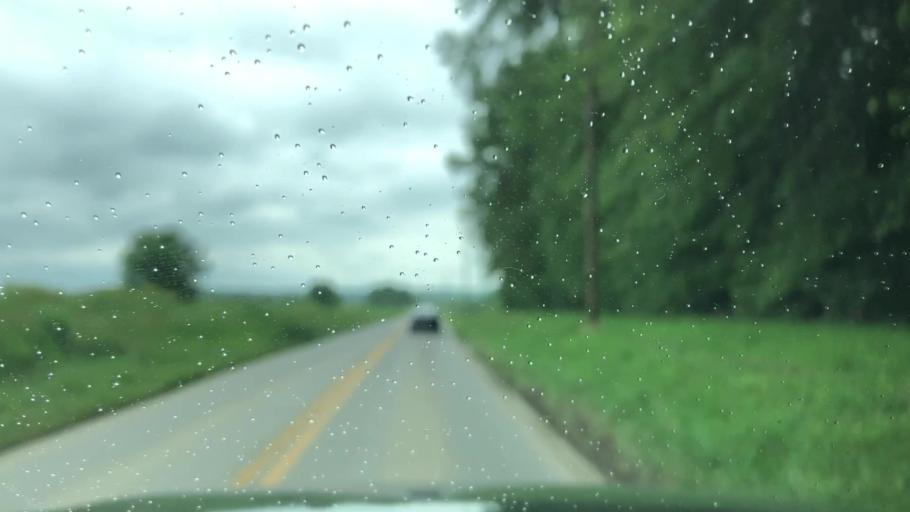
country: US
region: Missouri
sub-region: Saint Louis County
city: Bridgeton
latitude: 38.7977
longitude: -90.4176
